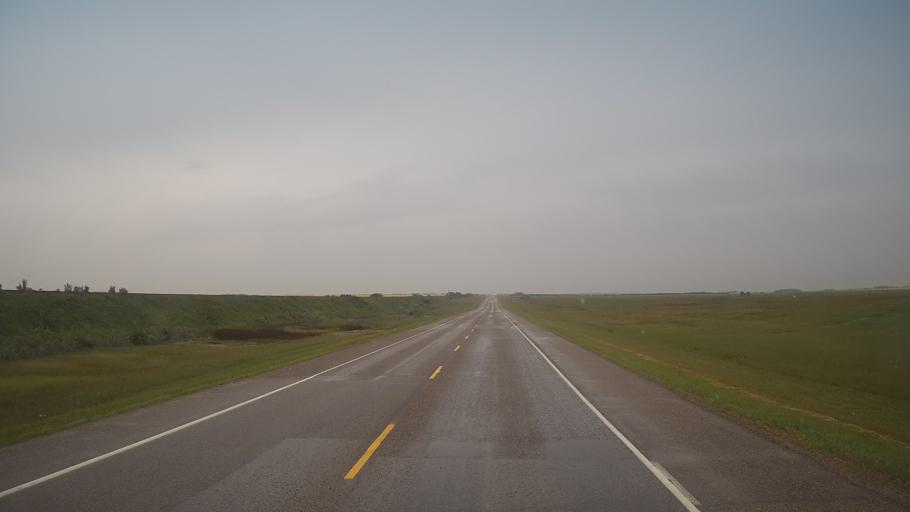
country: CA
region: Saskatchewan
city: Wilkie
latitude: 52.2138
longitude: -108.4987
